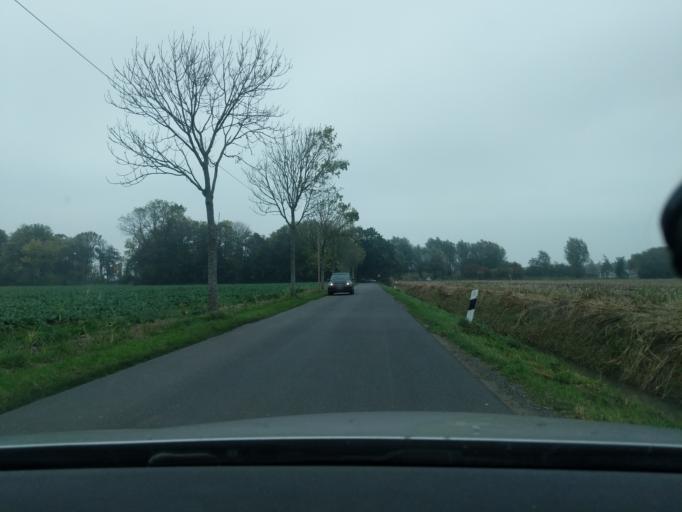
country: DE
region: Lower Saxony
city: Otterndorf
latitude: 53.8200
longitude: 8.8654
